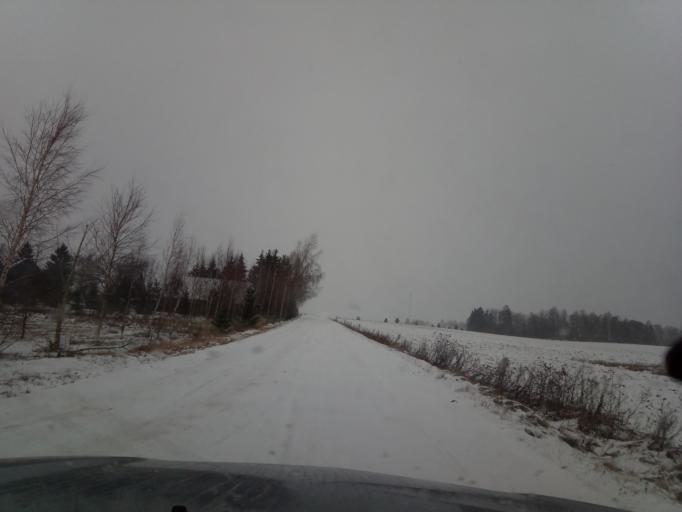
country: LT
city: Ramygala
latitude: 55.5629
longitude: 24.3503
